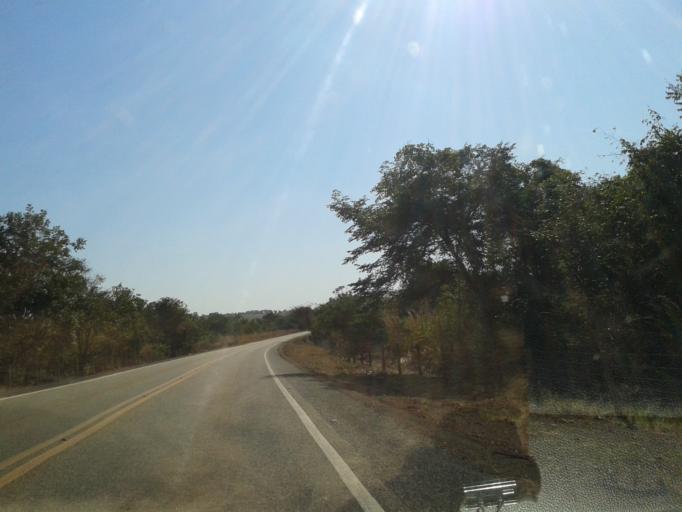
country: BR
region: Goias
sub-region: Mozarlandia
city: Mozarlandia
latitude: -14.6615
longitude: -50.5303
